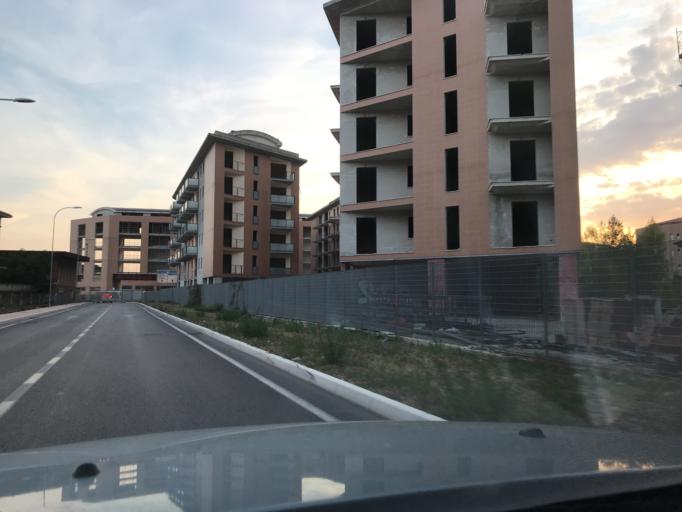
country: IT
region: Umbria
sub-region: Provincia di Perugia
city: Ponte Felcino
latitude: 43.0881
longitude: 12.4307
